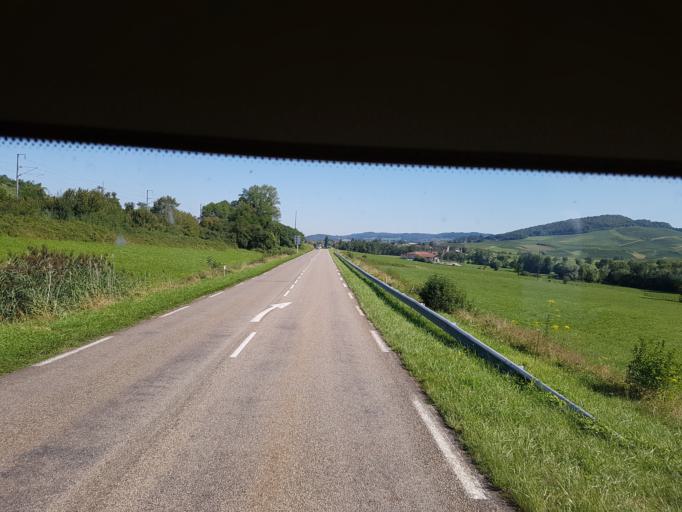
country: FR
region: Franche-Comte
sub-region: Departement du Jura
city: Perrigny
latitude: 46.7205
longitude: 5.5879
